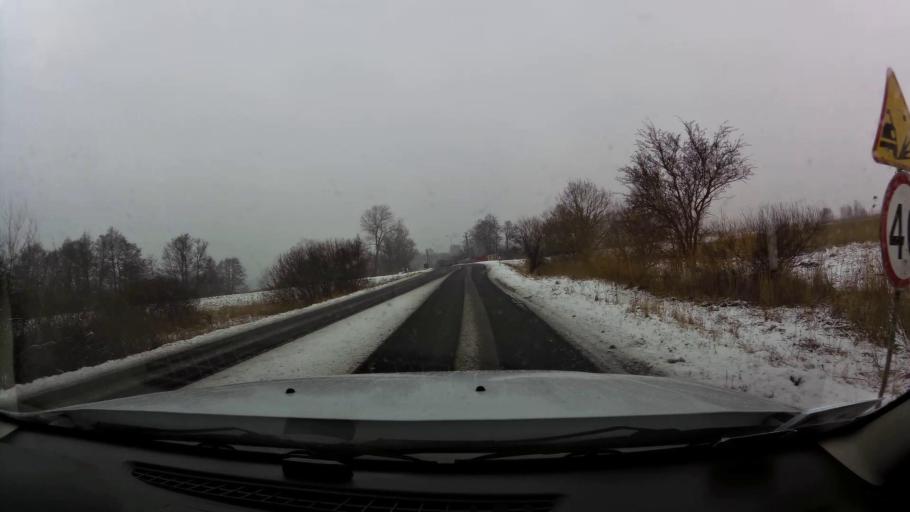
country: PL
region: West Pomeranian Voivodeship
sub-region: Powiat gryficki
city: Mrzezyno
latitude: 54.1337
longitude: 15.2829
